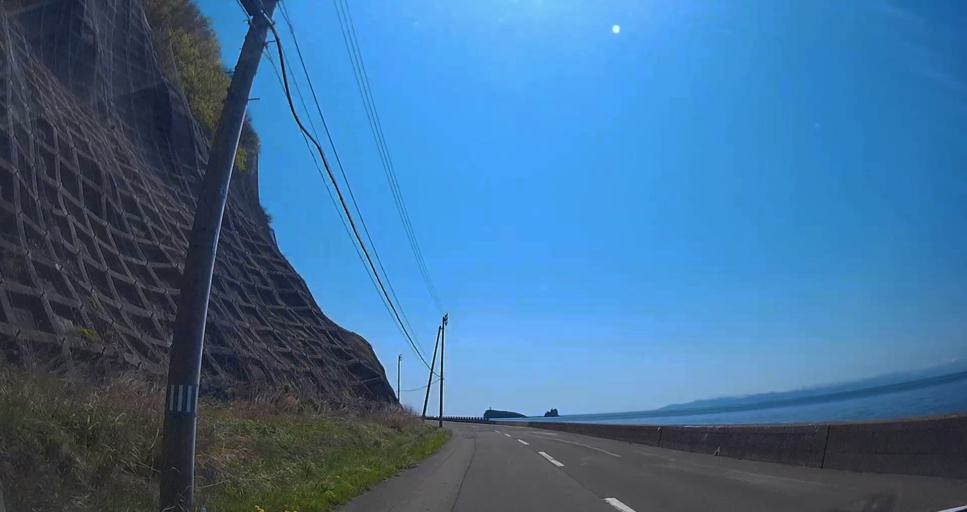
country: JP
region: Aomori
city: Aomori Shi
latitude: 41.1293
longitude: 140.7981
